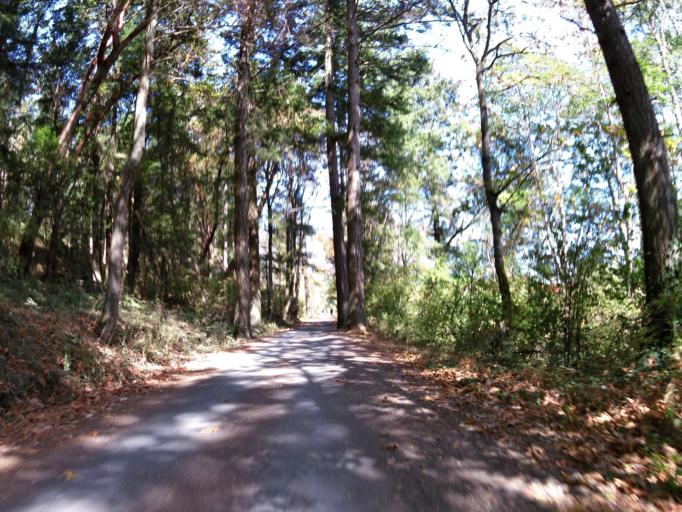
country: CA
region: British Columbia
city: Victoria
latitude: 48.4958
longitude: -123.3605
